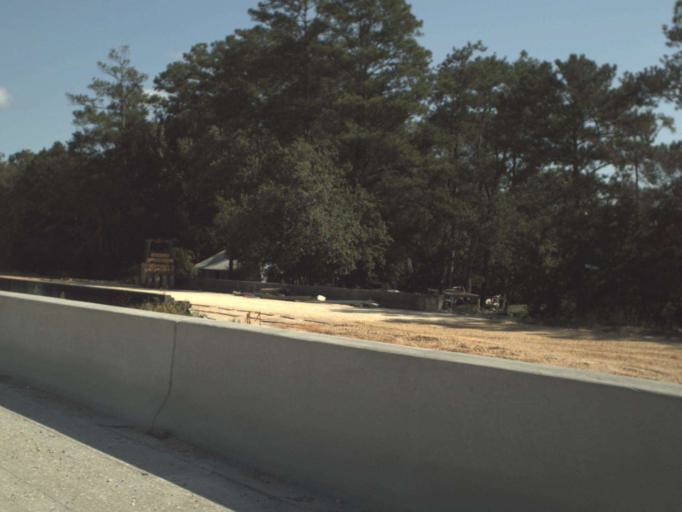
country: US
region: Florida
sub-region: Walton County
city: Freeport
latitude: 30.4694
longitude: -86.1299
